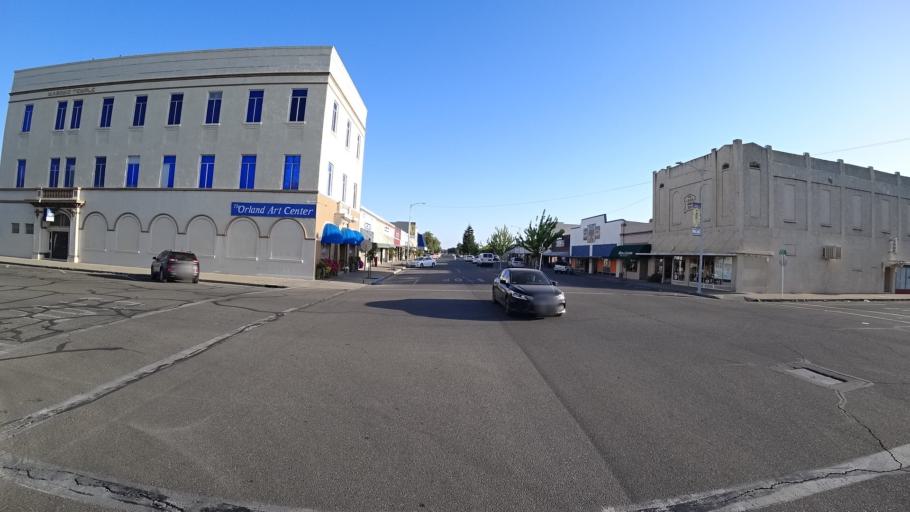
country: US
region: California
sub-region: Glenn County
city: Orland
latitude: 39.7462
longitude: -122.1943
